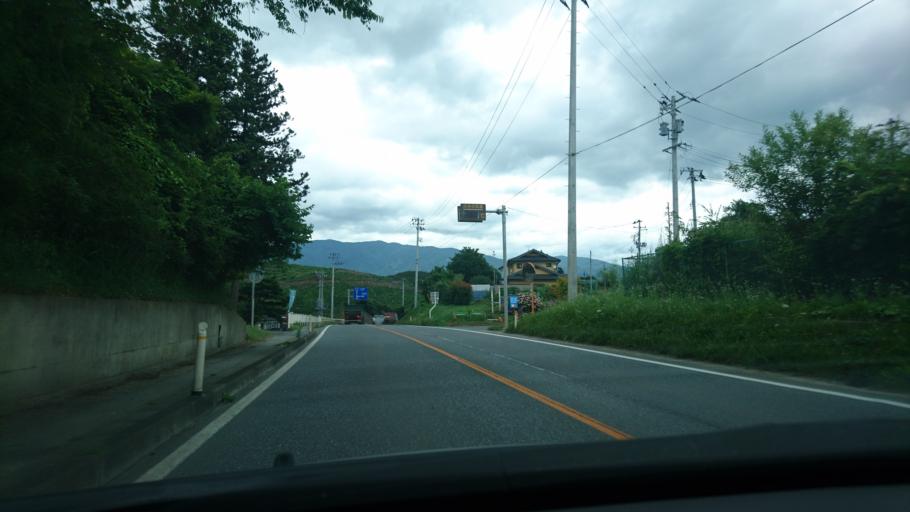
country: JP
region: Iwate
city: Ofunato
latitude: 38.9940
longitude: 141.6182
